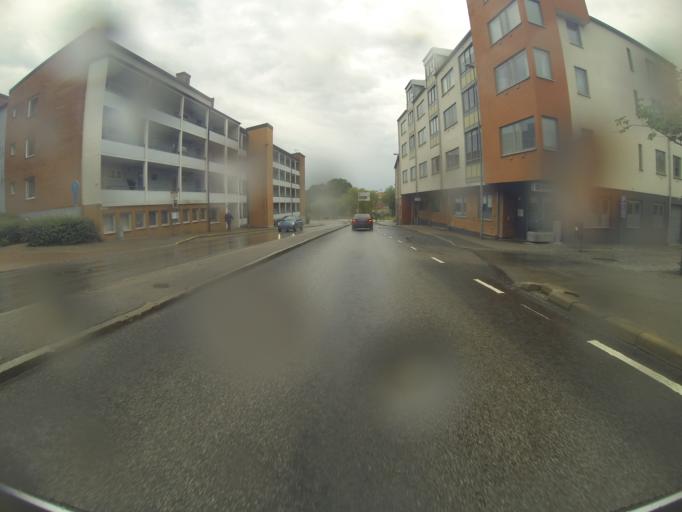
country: SE
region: Blekinge
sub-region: Ronneby Kommun
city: Ronneby
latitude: 56.2099
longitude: 15.2825
